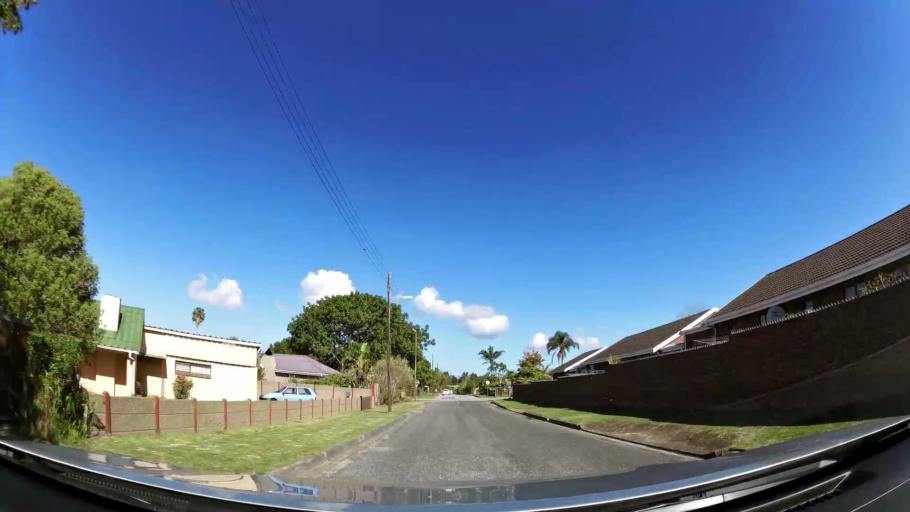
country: ZA
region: Western Cape
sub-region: Eden District Municipality
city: George
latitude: -33.9514
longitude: 22.4749
